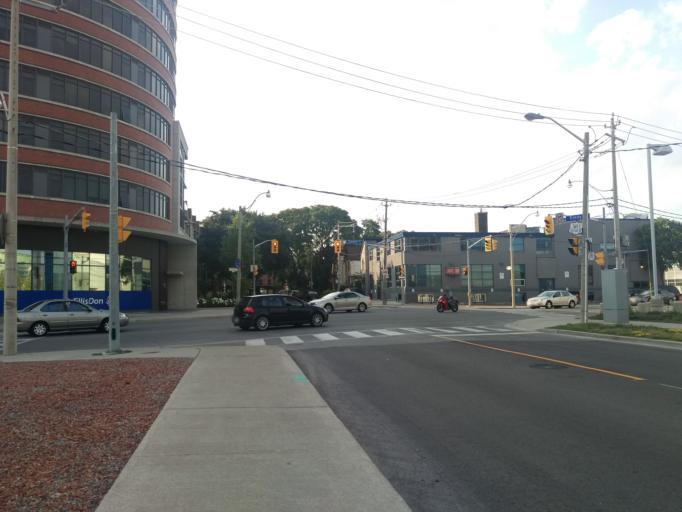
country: CA
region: Ontario
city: Toronto
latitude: 43.6522
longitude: -79.3605
